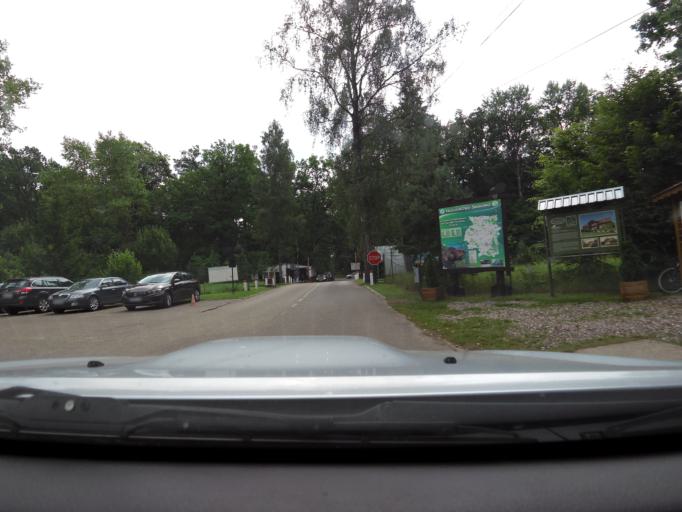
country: PL
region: Warmian-Masurian Voivodeship
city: Gierloz
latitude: 54.0796
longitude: 21.4930
